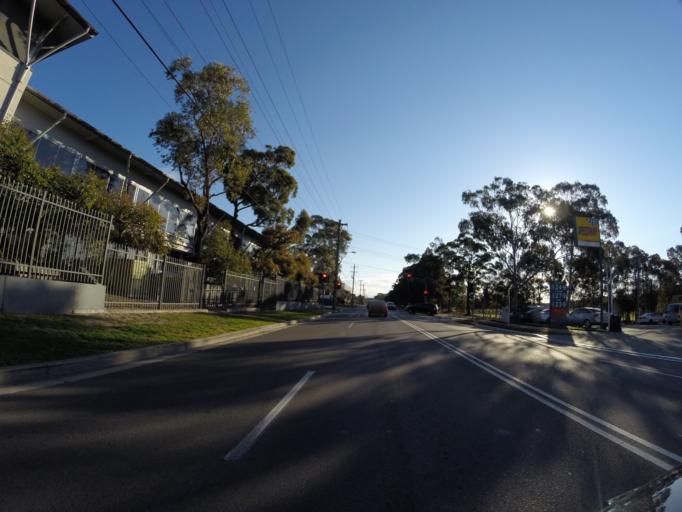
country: AU
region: New South Wales
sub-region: Fairfield
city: Fairfield East
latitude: -33.8699
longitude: 150.9807
